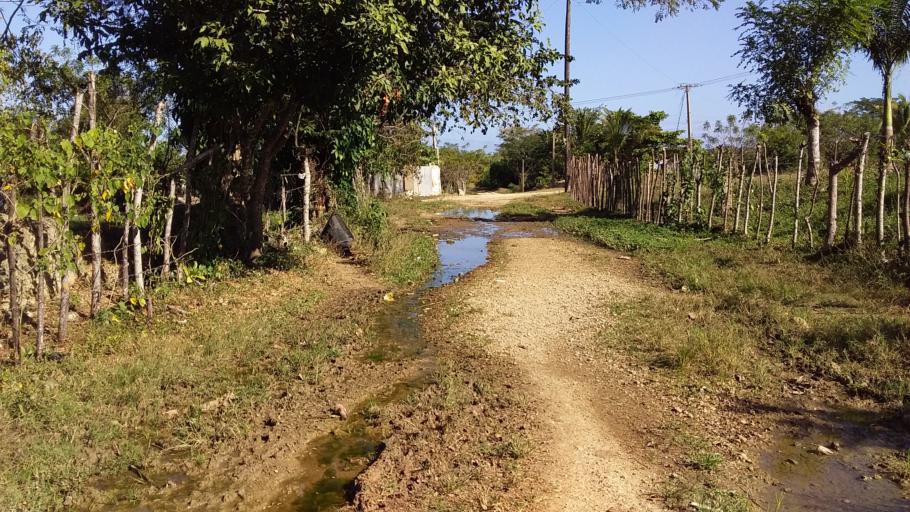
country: DO
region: Santo Domingo
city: Guerra
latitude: 18.5642
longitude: -69.7798
